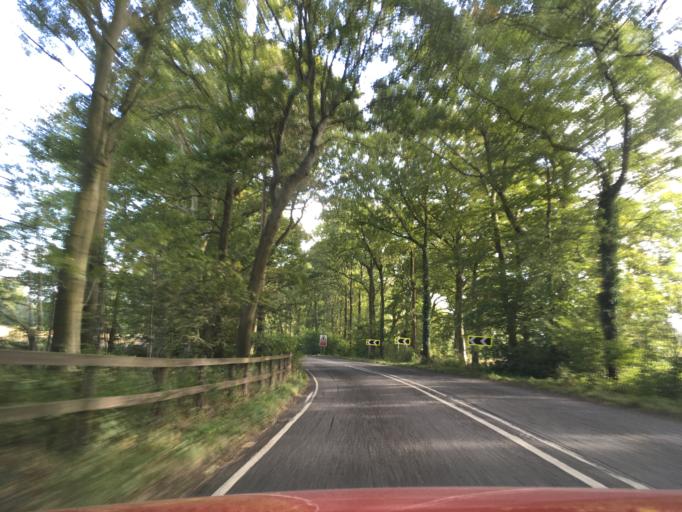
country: GB
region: England
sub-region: Hampshire
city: Old Basing
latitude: 51.2053
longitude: -1.0464
